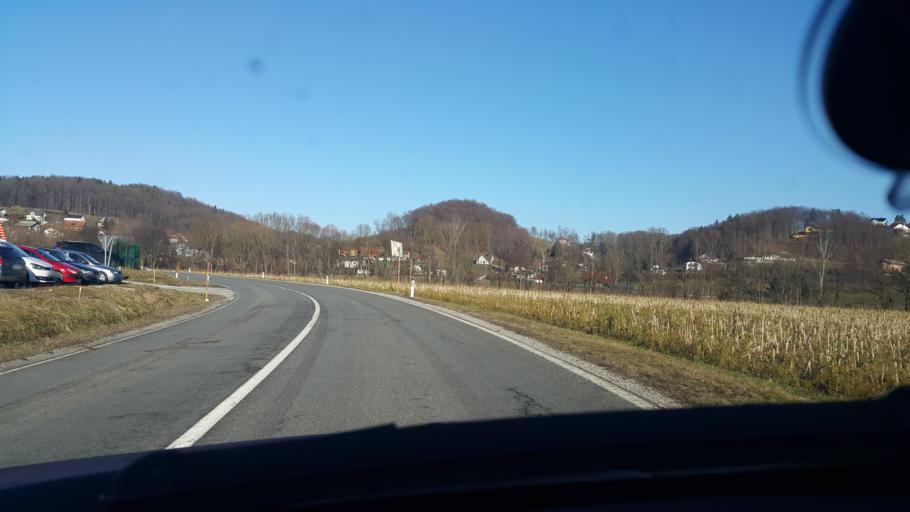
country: SI
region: Pesnica
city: Pesnica pri Mariboru
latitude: 46.6156
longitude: 15.6436
